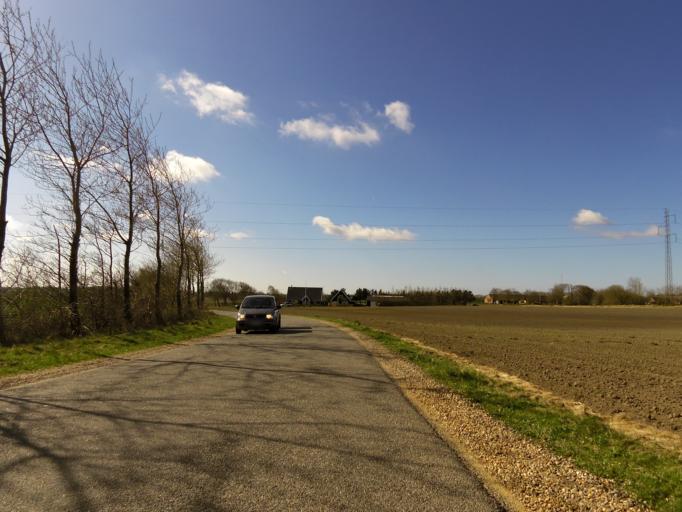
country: DK
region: Central Jutland
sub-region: Holstebro Kommune
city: Vinderup
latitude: 56.4465
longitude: 8.7214
